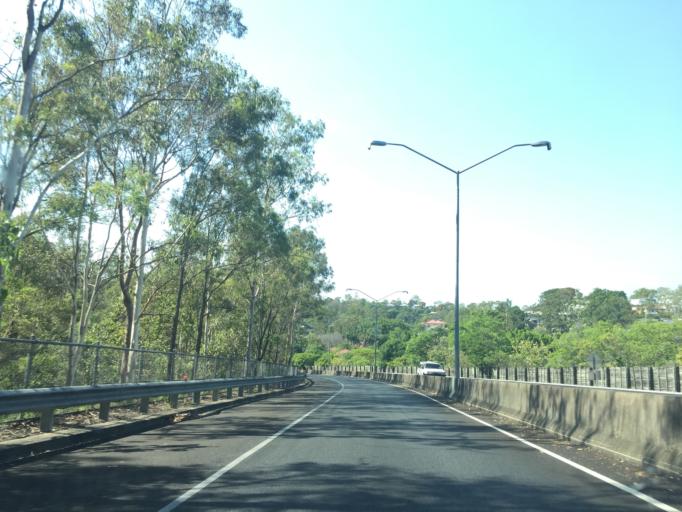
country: AU
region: Queensland
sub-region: Brisbane
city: Milton
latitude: -27.4624
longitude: 152.9882
